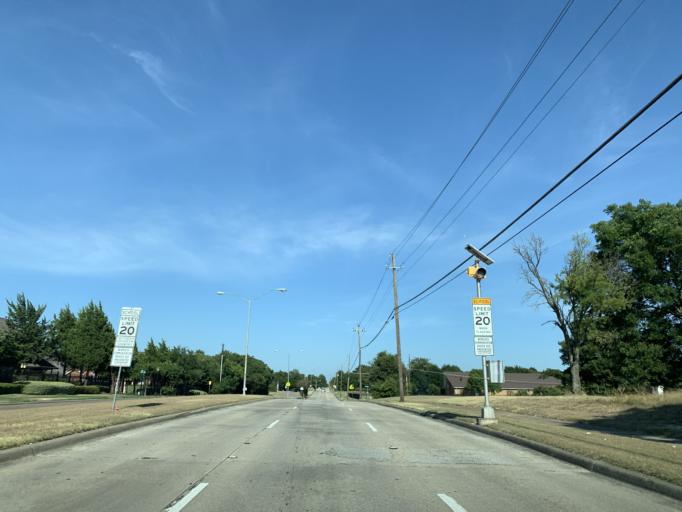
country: US
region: Texas
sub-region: Dallas County
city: Cockrell Hill
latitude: 32.7057
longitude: -96.8884
